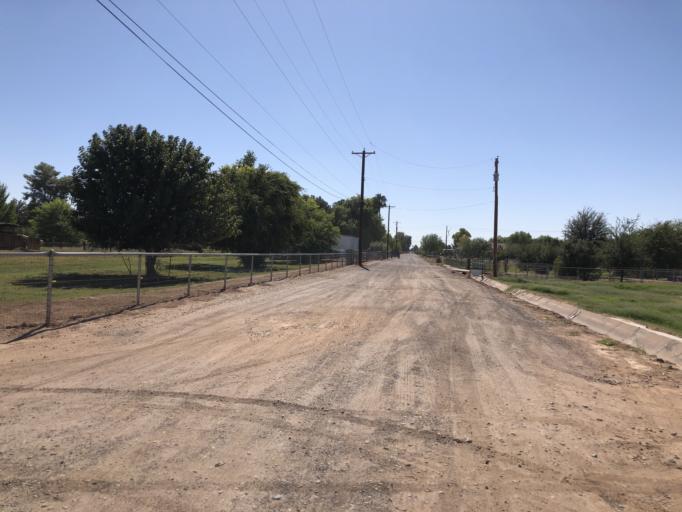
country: US
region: Arizona
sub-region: Maricopa County
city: Sun Lakes
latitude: 33.2280
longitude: -111.8152
